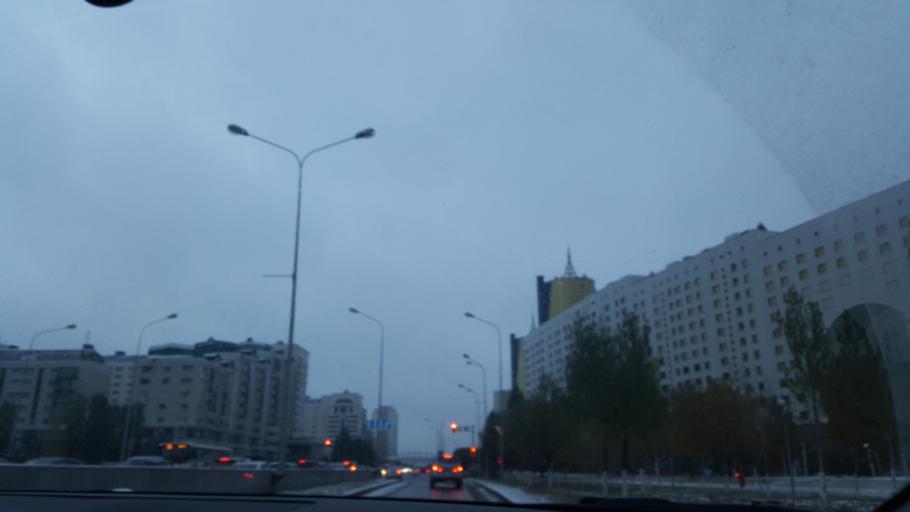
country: KZ
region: Astana Qalasy
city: Astana
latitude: 51.1236
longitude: 71.4373
